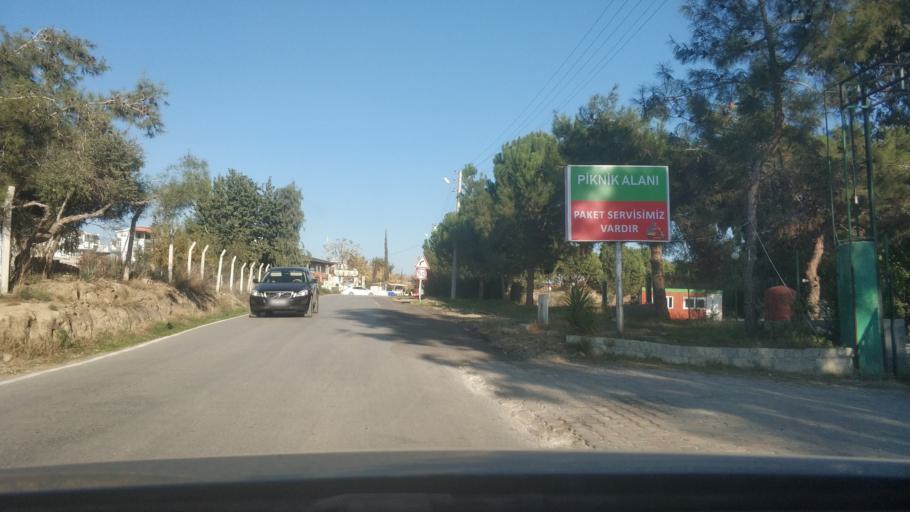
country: TR
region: Adana
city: Adana
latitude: 37.1052
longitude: 35.2961
